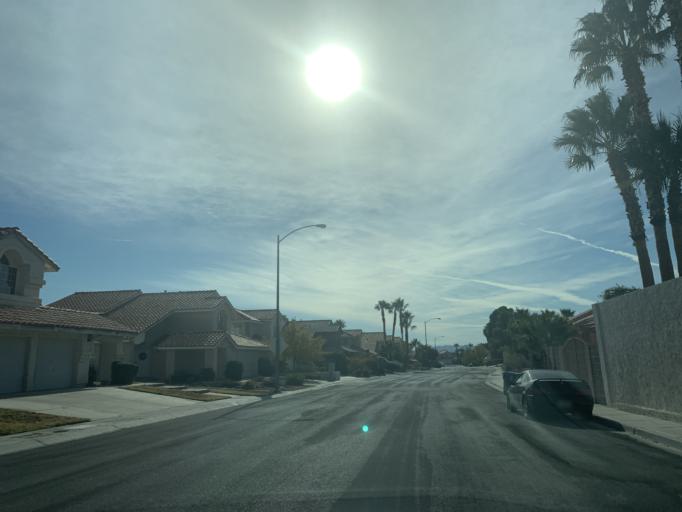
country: US
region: Nevada
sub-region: Clark County
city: Spring Valley
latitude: 36.1289
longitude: -115.2843
